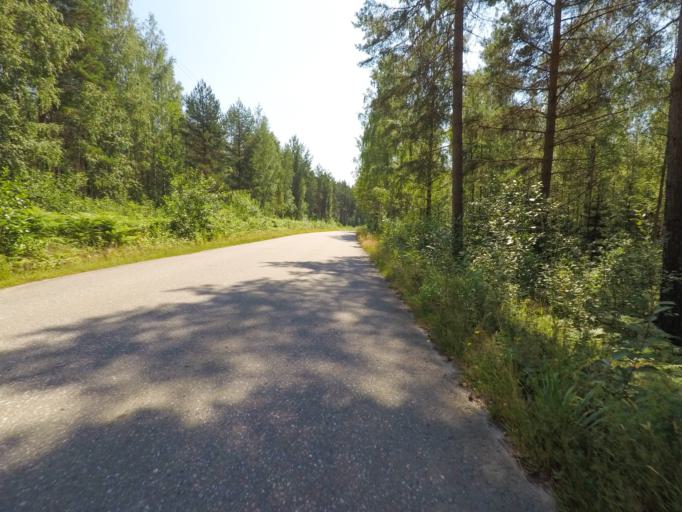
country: FI
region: Southern Savonia
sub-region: Mikkeli
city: Puumala
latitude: 61.4431
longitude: 28.1637
